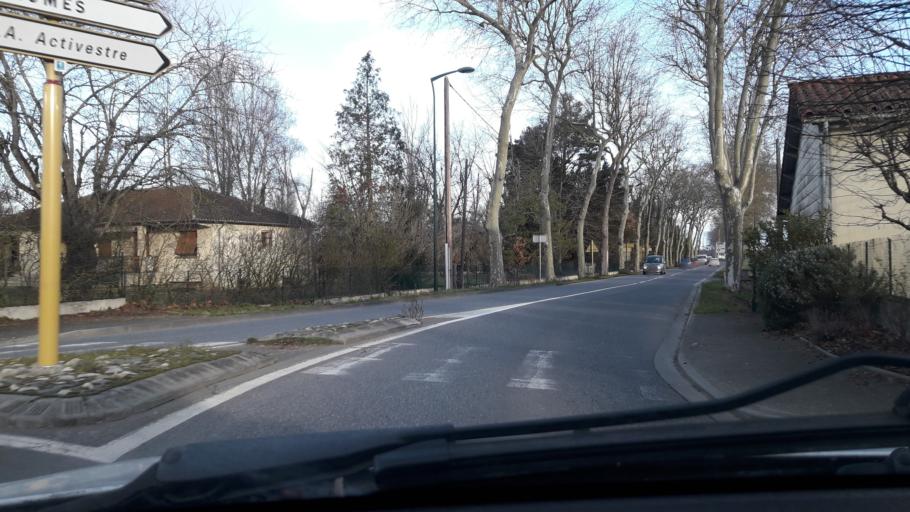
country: FR
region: Midi-Pyrenees
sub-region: Departement de la Haute-Garonne
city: Carbonne
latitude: 43.3145
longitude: 1.2214
